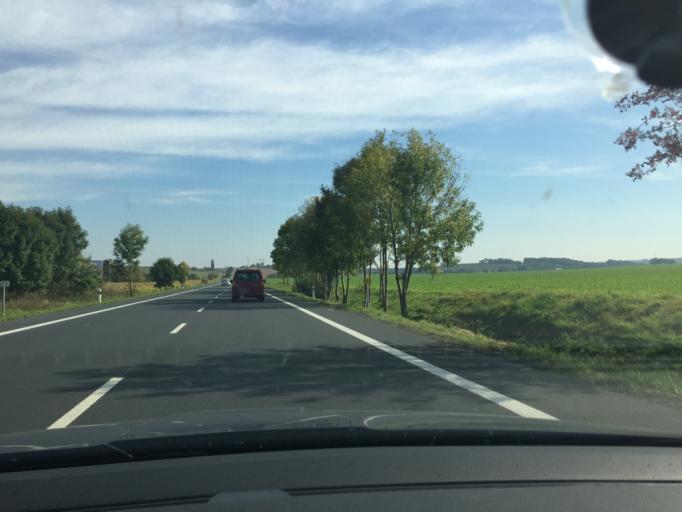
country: CZ
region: Central Bohemia
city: Planany
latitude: 50.0454
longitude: 15.0407
